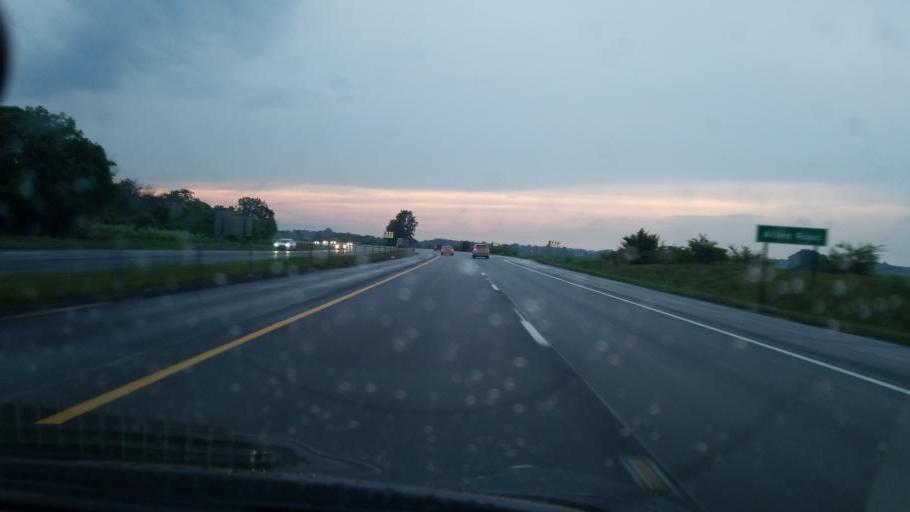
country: US
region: Ohio
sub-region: Fairfield County
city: Pickerington
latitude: 39.8242
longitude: -82.7194
